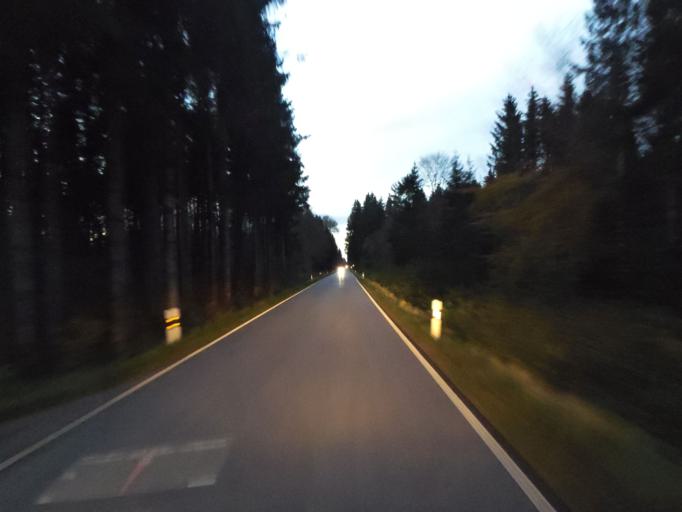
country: DE
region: Bavaria
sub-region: Upper Bavaria
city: Aying
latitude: 47.9647
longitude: 11.7350
